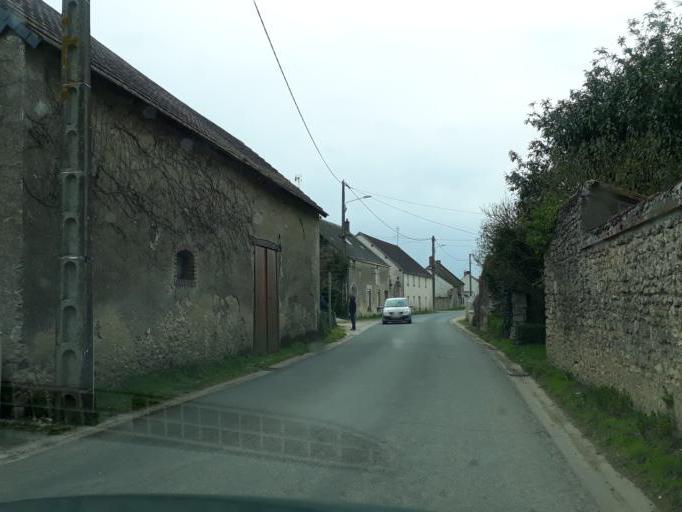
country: FR
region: Centre
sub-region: Departement du Loir-et-Cher
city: Villebarou
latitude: 47.6413
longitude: 1.2970
